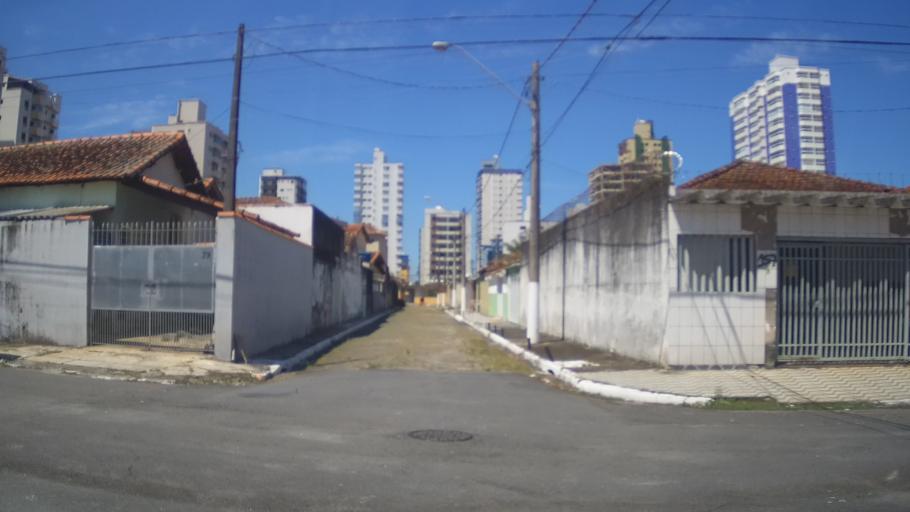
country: BR
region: Sao Paulo
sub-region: Praia Grande
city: Praia Grande
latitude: -24.0130
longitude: -46.4344
